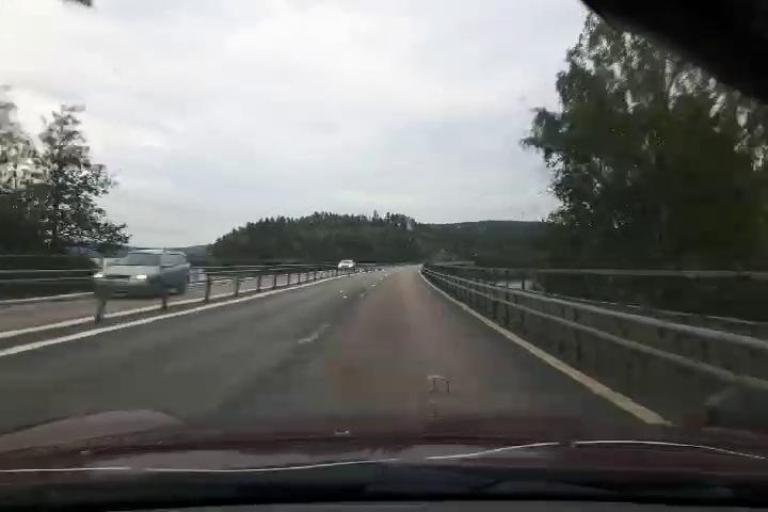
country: SE
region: Vaesternorrland
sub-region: Haernoesands Kommun
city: Haernoesand
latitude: 62.8157
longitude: 17.9676
